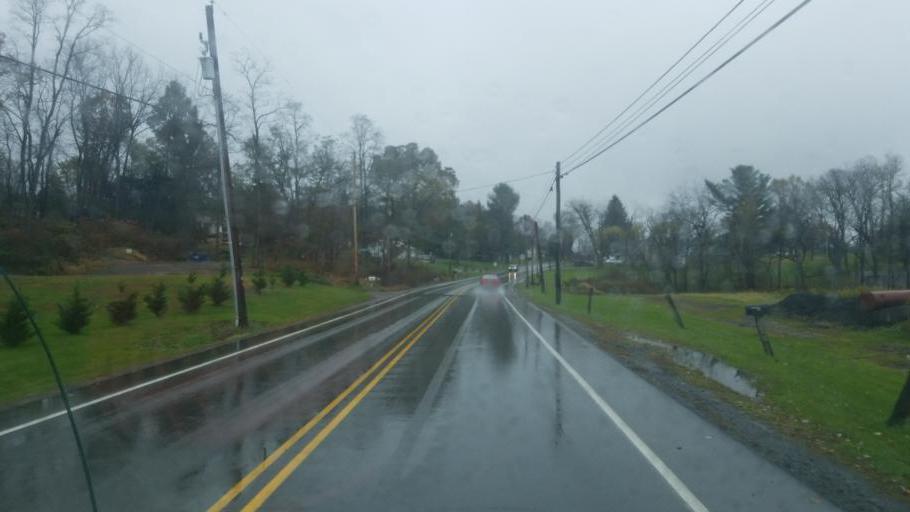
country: US
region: Pennsylvania
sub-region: Clinton County
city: Mill Hall
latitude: 41.1038
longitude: -77.5120
